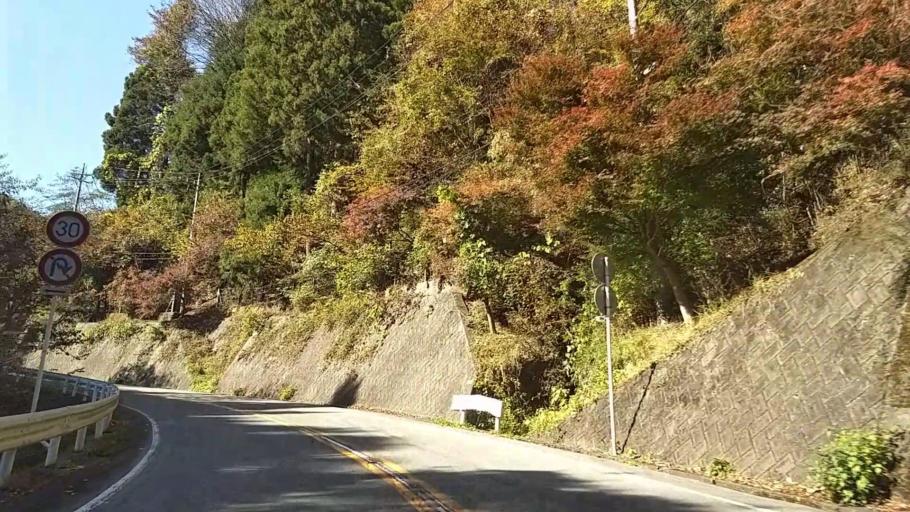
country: JP
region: Yamanashi
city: Otsuki
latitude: 35.7293
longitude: 138.9831
